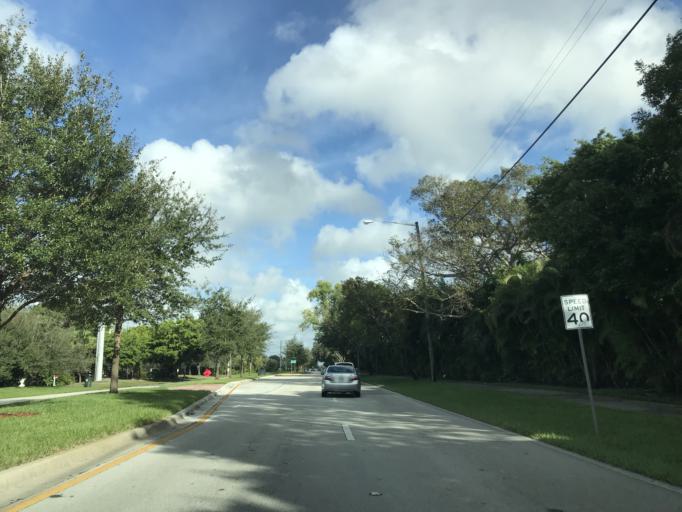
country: US
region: Florida
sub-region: Broward County
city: Coconut Creek
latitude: 26.2657
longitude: -80.1863
